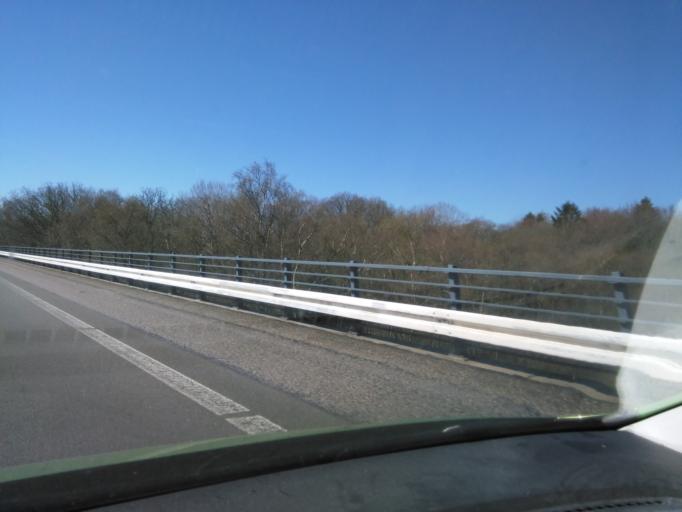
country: DK
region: South Denmark
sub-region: Varde Kommune
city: Varde
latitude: 55.6796
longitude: 8.5819
